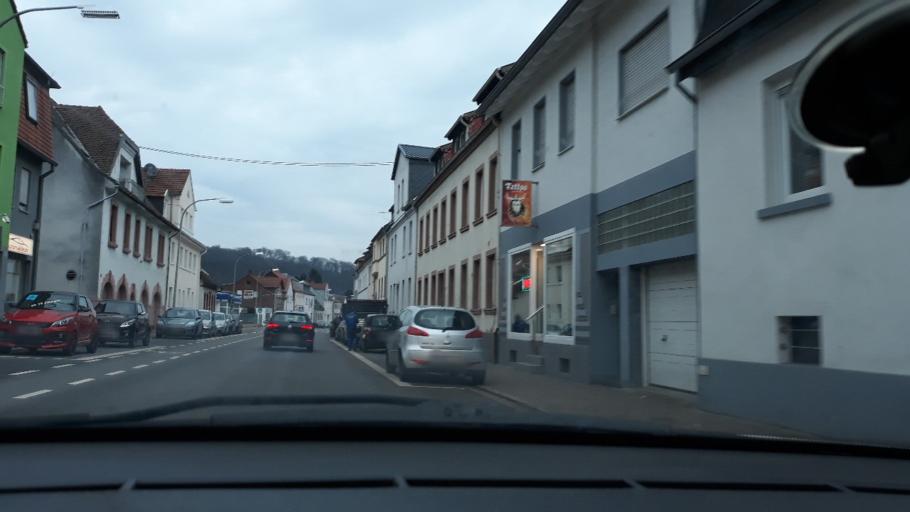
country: DE
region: Saarland
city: Sulzbach
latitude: 49.2473
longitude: 7.0603
